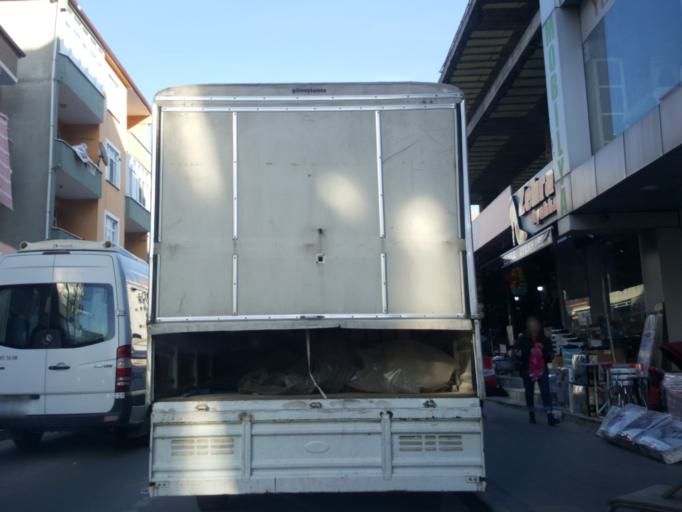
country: TR
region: Kocaeli
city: Tavsancil
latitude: 40.7853
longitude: 29.5421
